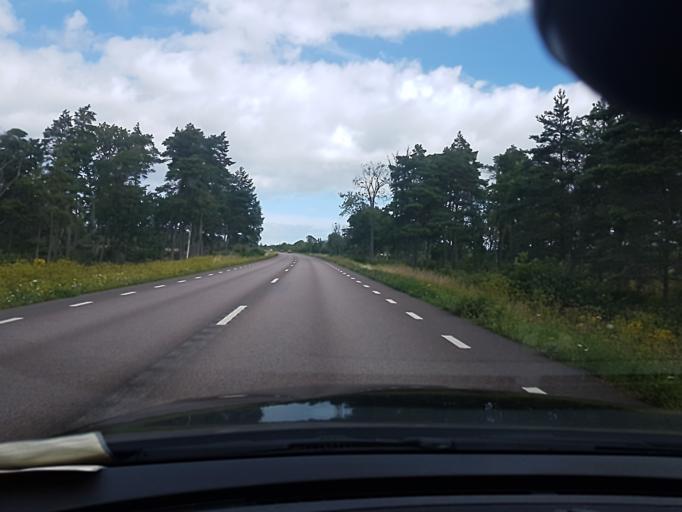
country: SE
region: Kalmar
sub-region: Borgholms Kommun
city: Borgholm
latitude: 57.0828
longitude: 16.9203
